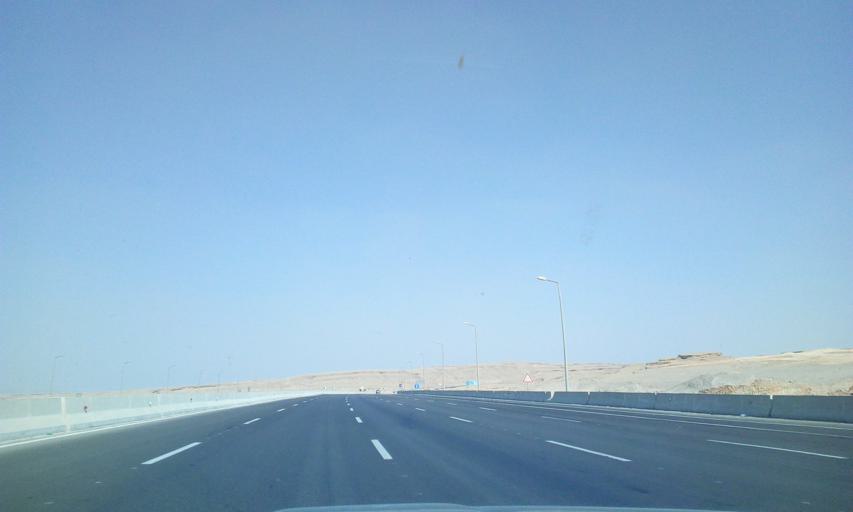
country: EG
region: As Suways
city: Ain Sukhna
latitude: 29.7608
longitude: 31.9980
